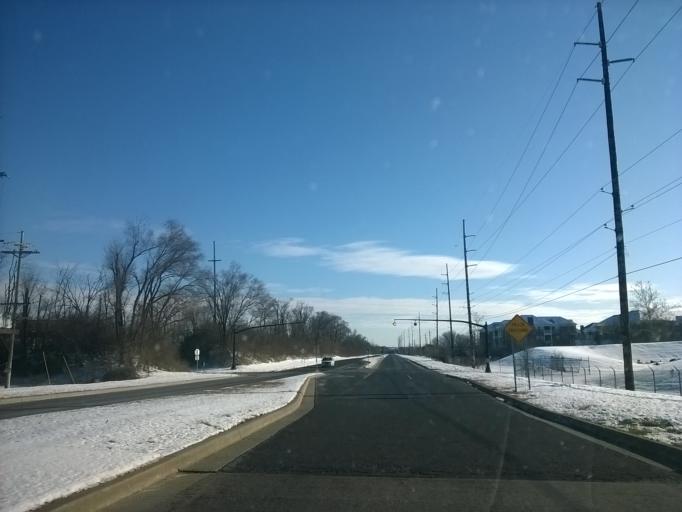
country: US
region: Indiana
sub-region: Hamilton County
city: Carmel
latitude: 39.9355
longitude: -86.0888
